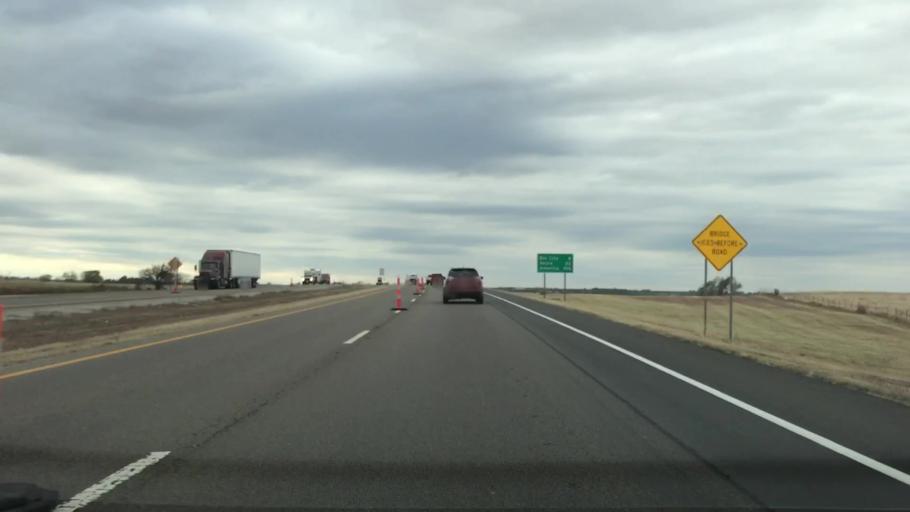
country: US
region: Oklahoma
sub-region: Beckham County
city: Elk City
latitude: 35.4262
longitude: -99.2902
